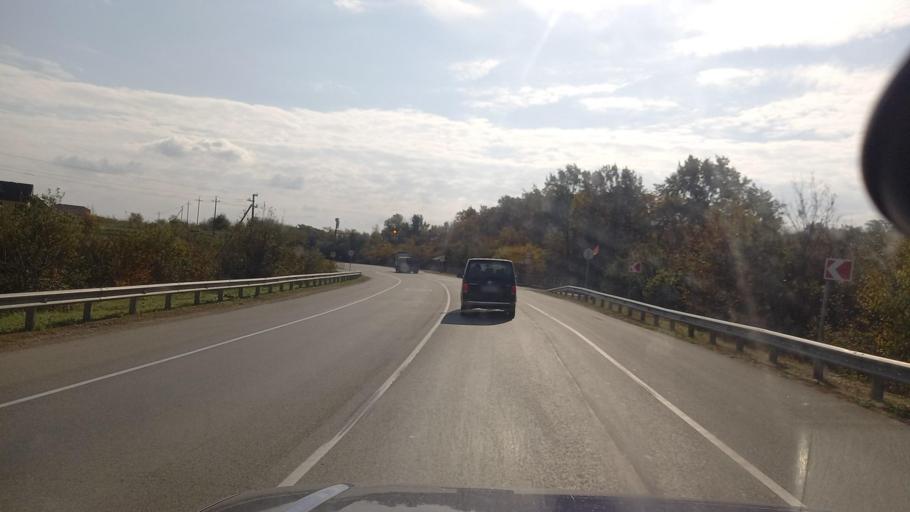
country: RU
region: Krasnodarskiy
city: Abinsk
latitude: 44.8506
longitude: 38.1357
